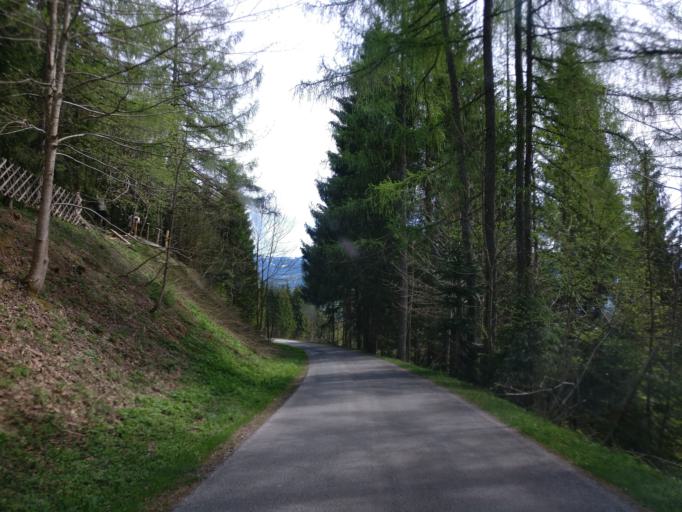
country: AT
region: Salzburg
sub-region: Politischer Bezirk Sankt Johann im Pongau
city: Pfarrwerfen
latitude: 47.4773
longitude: 13.2131
